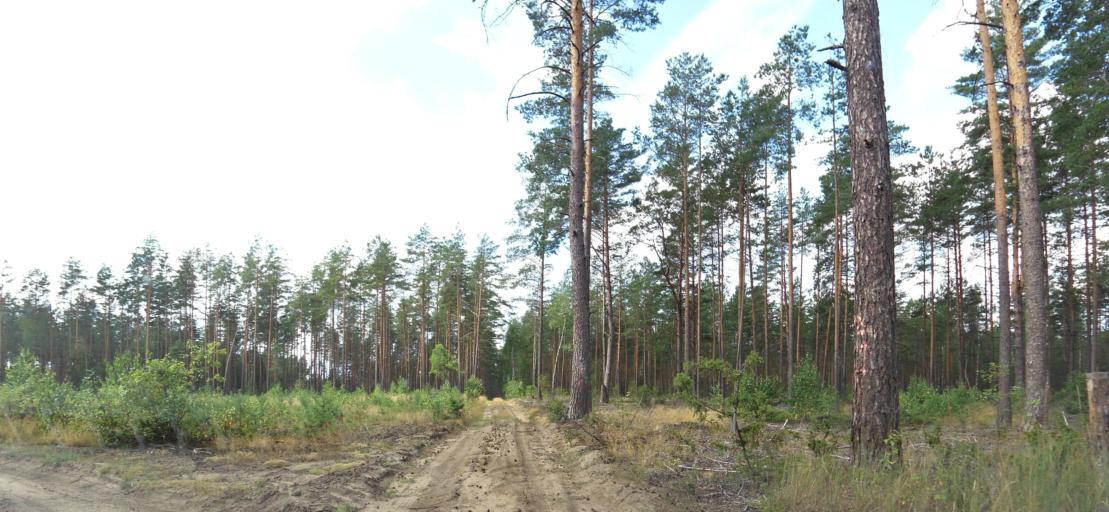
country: LT
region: Alytaus apskritis
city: Varena
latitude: 54.2436
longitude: 24.6555
